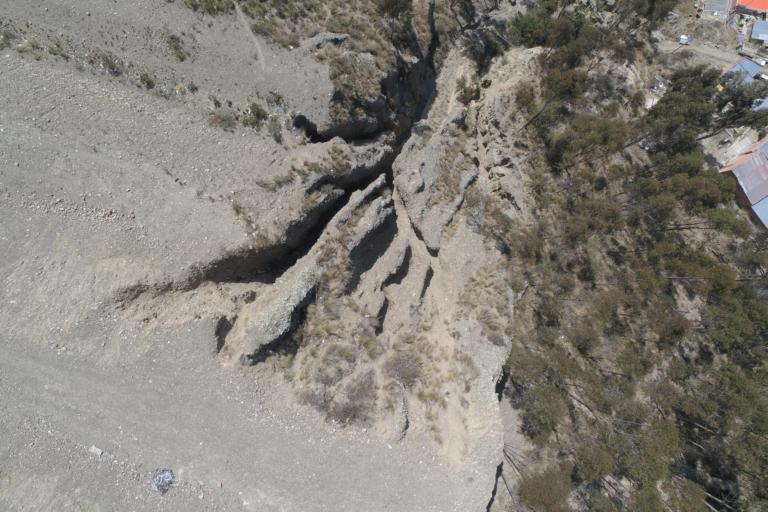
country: BO
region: La Paz
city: La Paz
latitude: -16.4975
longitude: -68.0998
